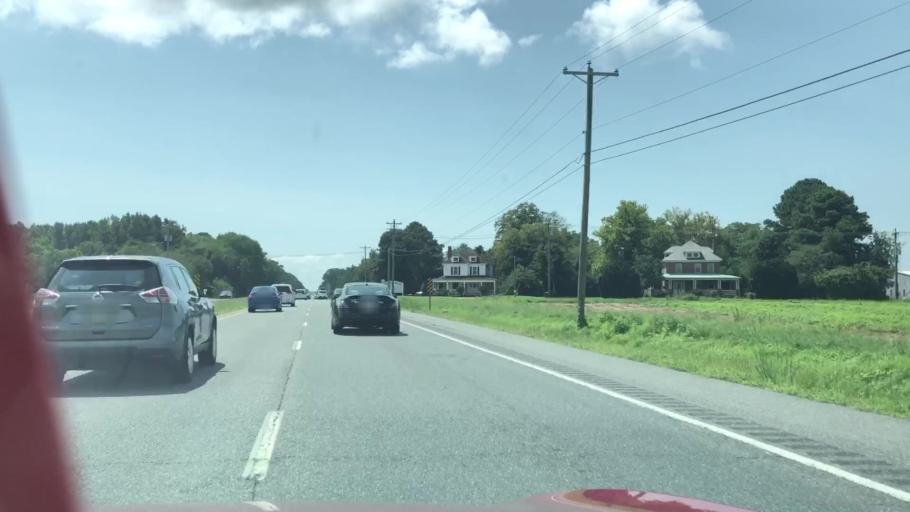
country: US
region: Virginia
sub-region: Northampton County
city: Cape Charles
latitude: 37.2086
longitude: -75.9662
